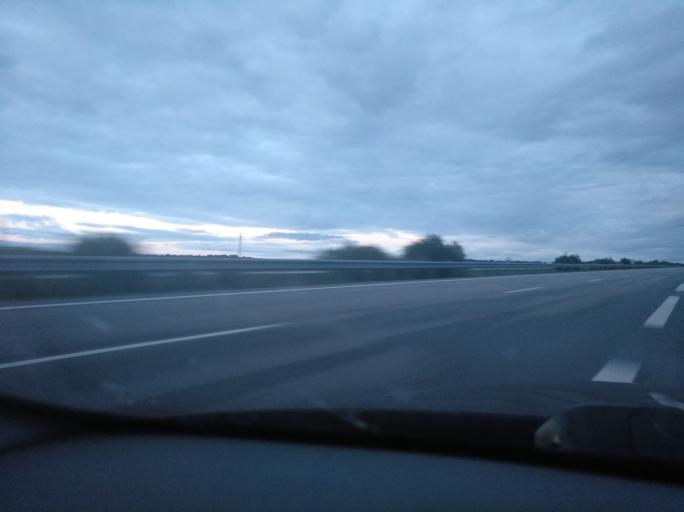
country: PT
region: Portalegre
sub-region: Elvas
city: Elvas
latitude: 38.8725
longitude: -7.2736
